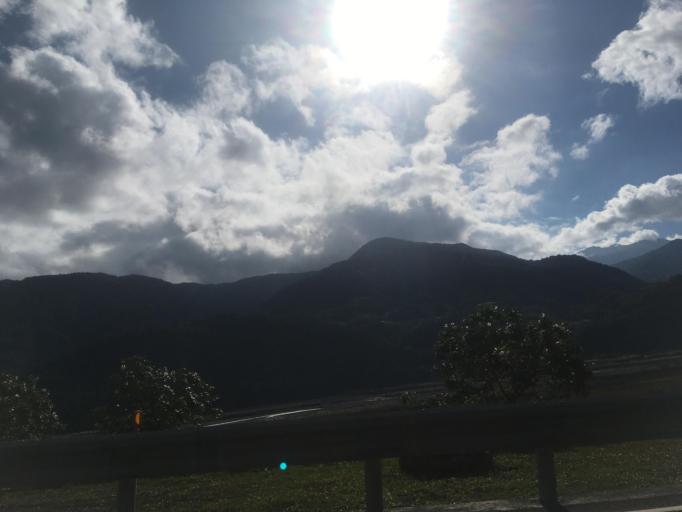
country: TW
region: Taiwan
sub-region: Yilan
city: Yilan
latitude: 24.6178
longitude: 121.5331
